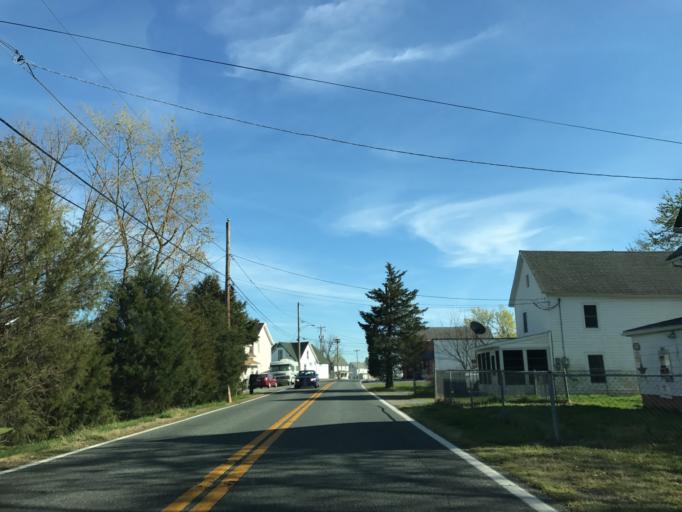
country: US
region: Maryland
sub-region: Caroline County
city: Greensboro
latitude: 39.0351
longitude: -75.7870
